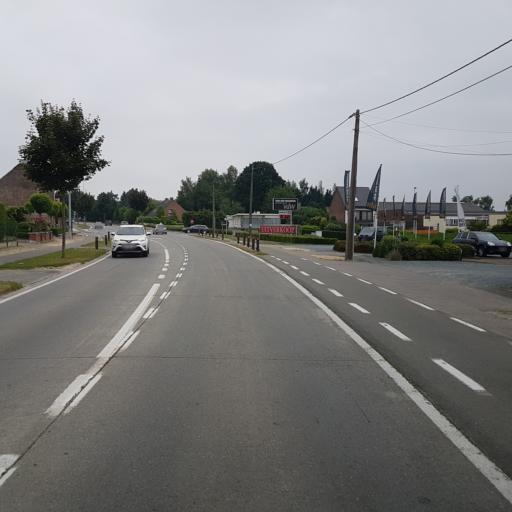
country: BE
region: Flanders
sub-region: Provincie Oost-Vlaanderen
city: Denderleeuw
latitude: 50.8843
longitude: 4.0636
